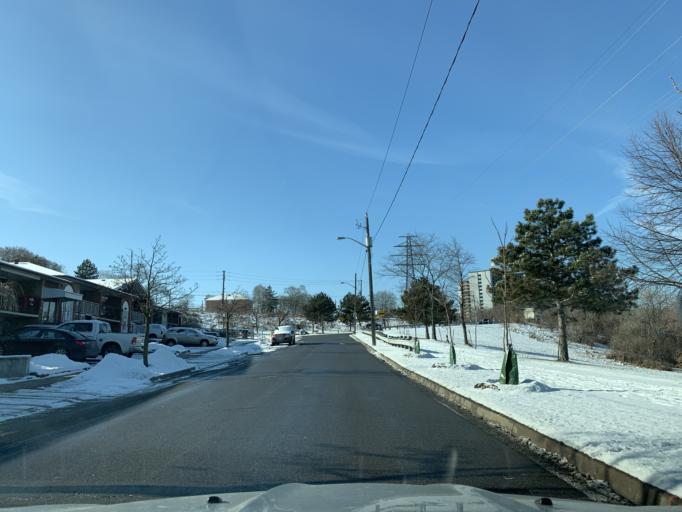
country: CA
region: Ontario
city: Toronto
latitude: 43.6727
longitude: -79.4854
